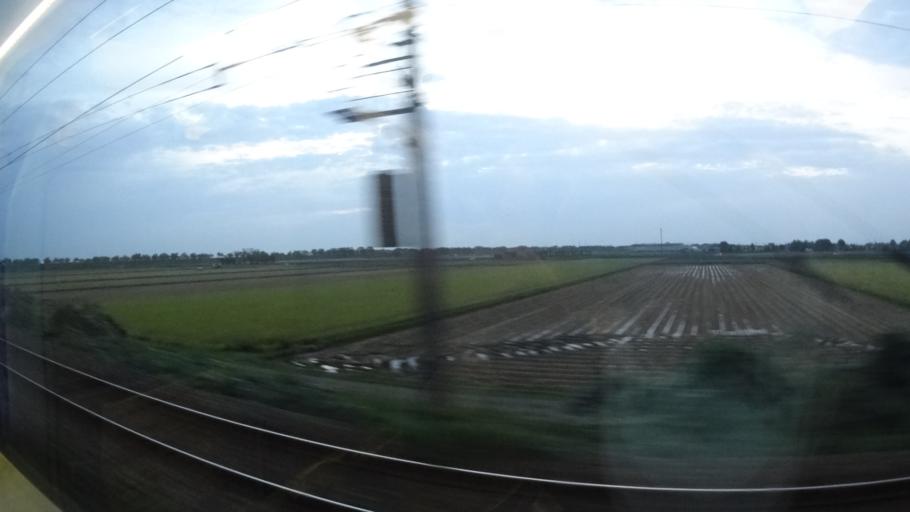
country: JP
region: Niigata
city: Shibata
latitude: 37.9692
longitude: 139.3548
